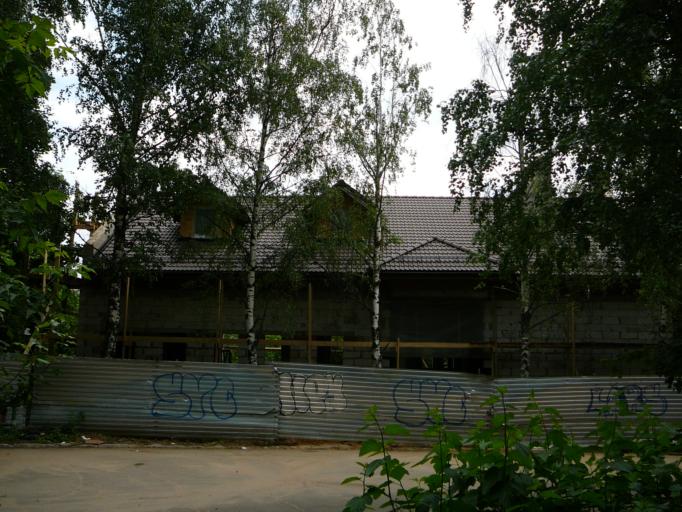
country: RU
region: Moskovskaya
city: Krasnogorsk
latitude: 55.8178
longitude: 37.3255
